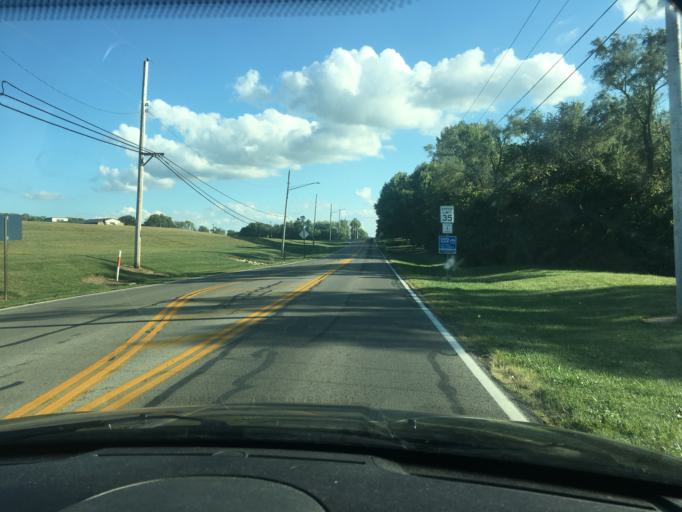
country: US
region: Ohio
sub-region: Logan County
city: Bellefontaine
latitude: 40.3460
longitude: -83.7487
